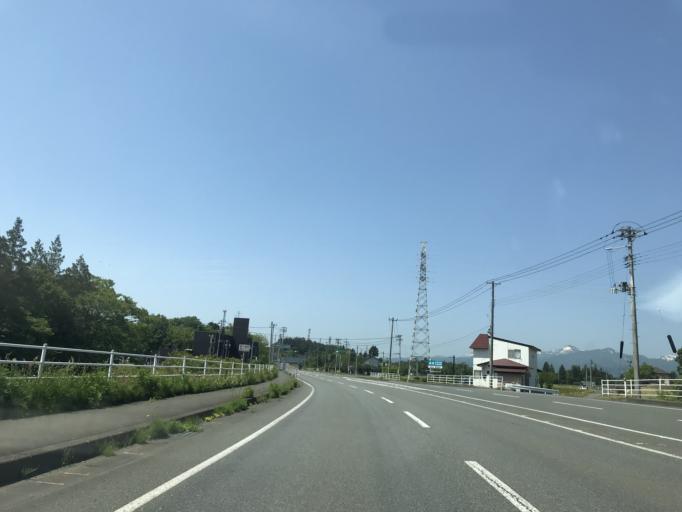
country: JP
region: Iwate
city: Kitakami
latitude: 39.2234
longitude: 141.0929
